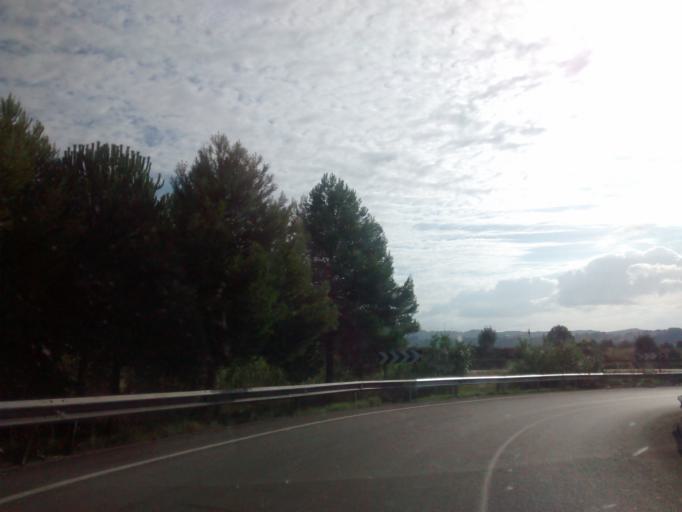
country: ES
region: Catalonia
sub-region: Provincia de Barcelona
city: Abrera
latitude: 41.5037
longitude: 1.9080
